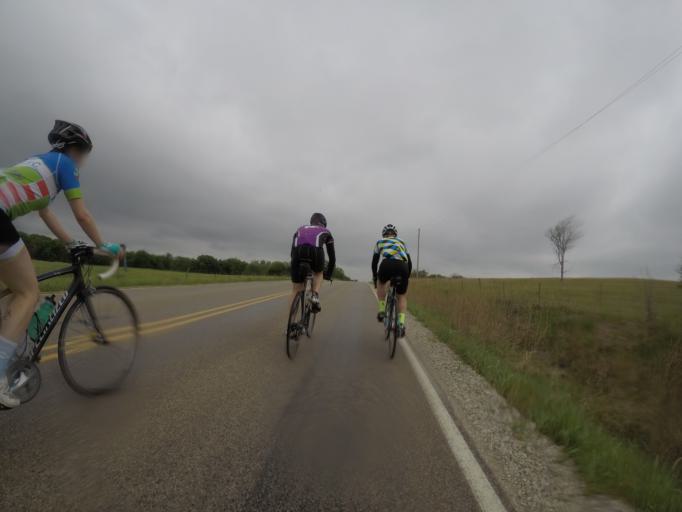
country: US
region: Kansas
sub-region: Pottawatomie County
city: Westmoreland
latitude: 39.4745
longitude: -96.1839
